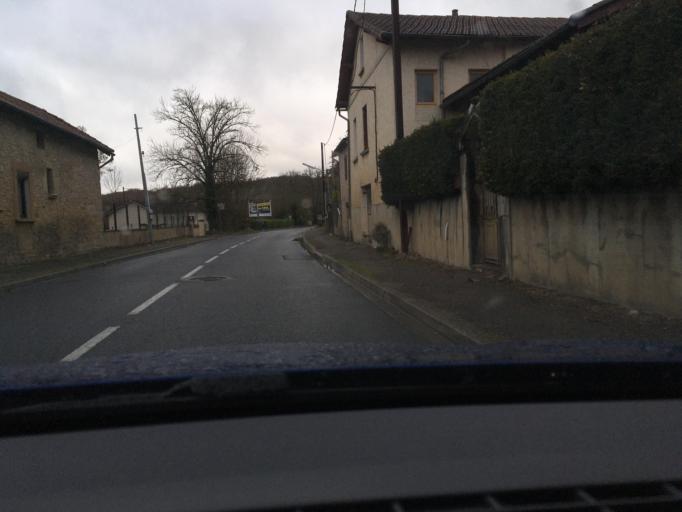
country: FR
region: Midi-Pyrenees
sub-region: Departement de l'Aveyron
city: Villefranche-de-Rouergue
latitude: 44.3630
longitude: 2.0199
